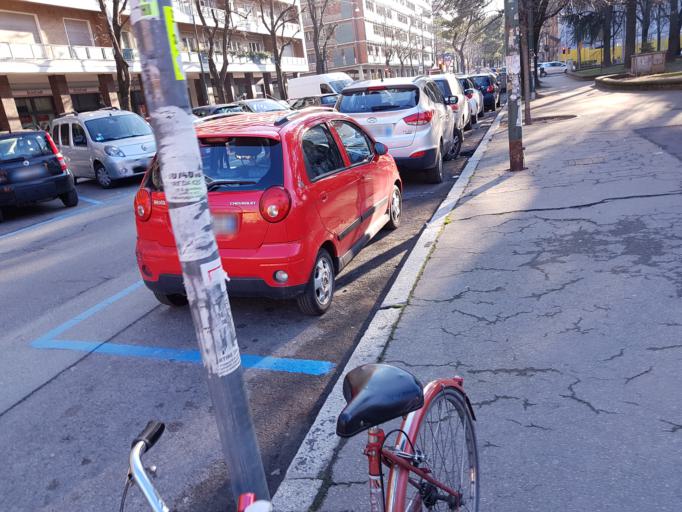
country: IT
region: Emilia-Romagna
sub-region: Provincia di Bologna
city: Bologna
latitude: 44.4877
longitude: 11.3620
